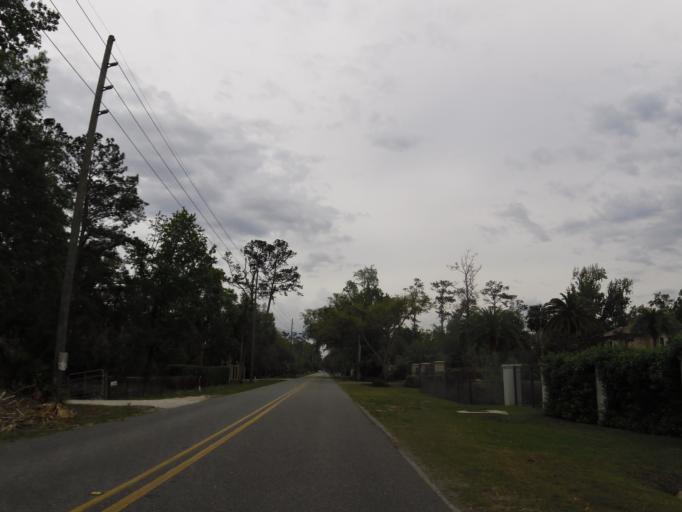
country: US
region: Florida
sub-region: Saint Johns County
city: Palm Valley
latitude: 30.2050
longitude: -81.4074
